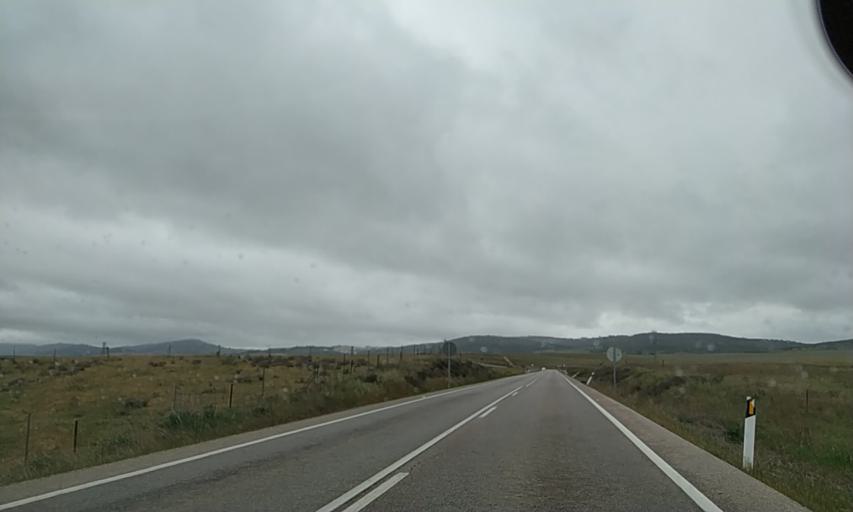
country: ES
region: Extremadura
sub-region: Provincia de Caceres
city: Casar de Caceres
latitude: 39.5227
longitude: -6.3982
